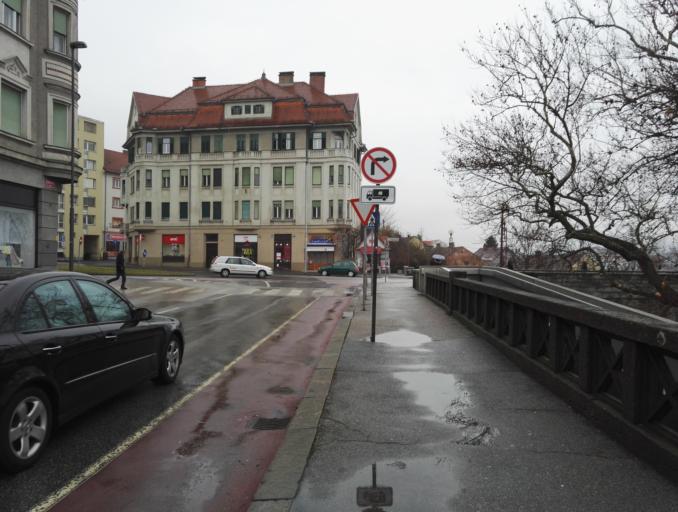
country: SI
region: Maribor
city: Maribor
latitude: 46.5546
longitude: 15.6465
